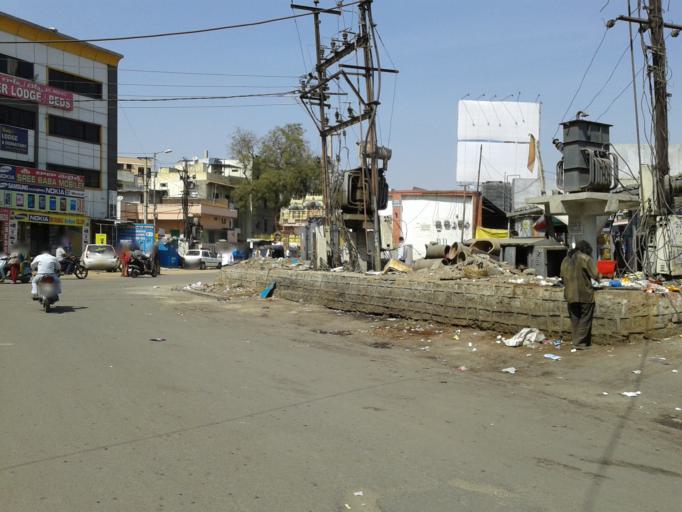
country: IN
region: Telangana
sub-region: Hyderabad
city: Malkajgiri
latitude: 17.4358
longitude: 78.5001
